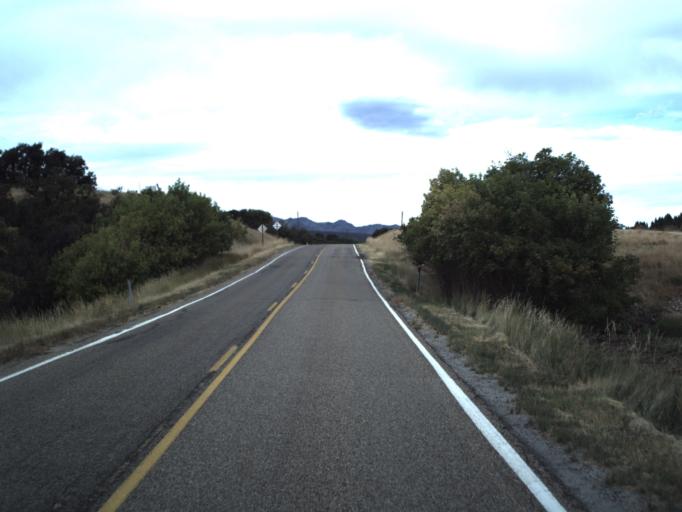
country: US
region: Utah
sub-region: Morgan County
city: Morgan
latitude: 40.9504
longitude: -111.6584
